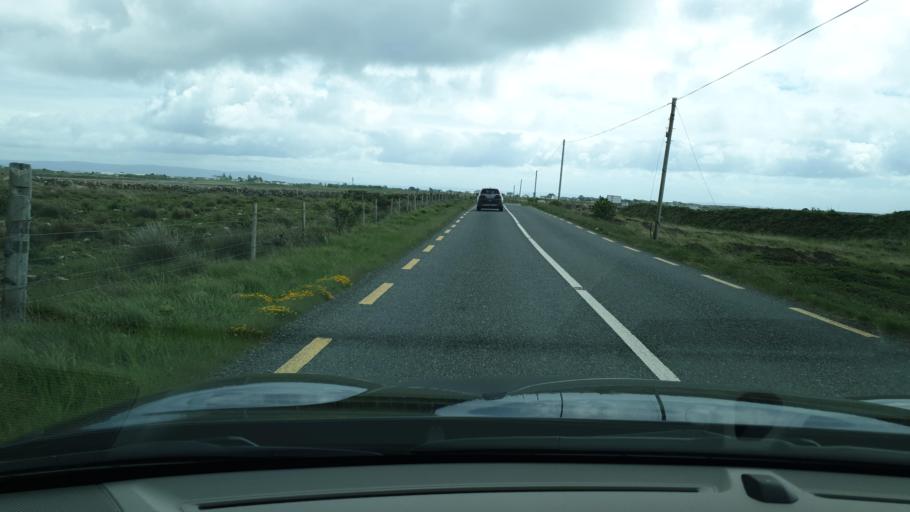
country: IE
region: Connaught
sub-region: County Galway
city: Oughterard
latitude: 53.2521
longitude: -9.5078
